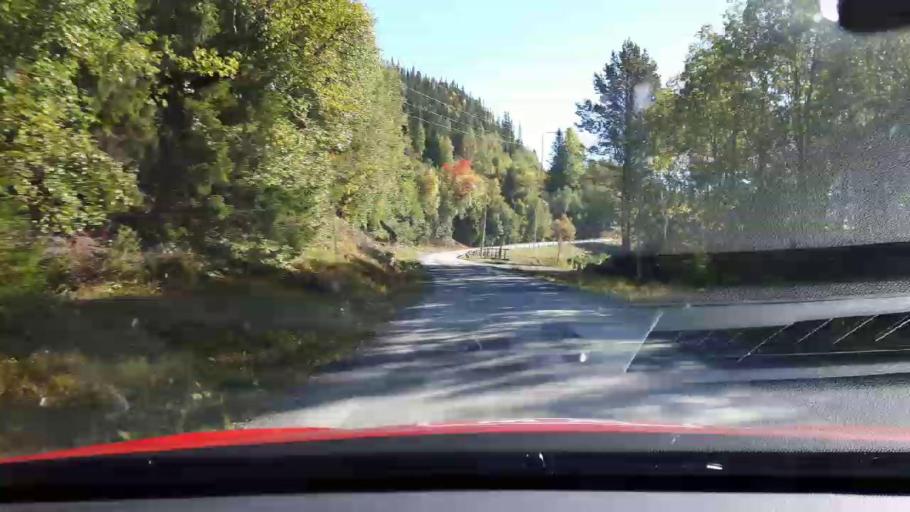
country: NO
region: Nord-Trondelag
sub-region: Lierne
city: Sandvika
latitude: 64.6471
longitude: 13.7612
